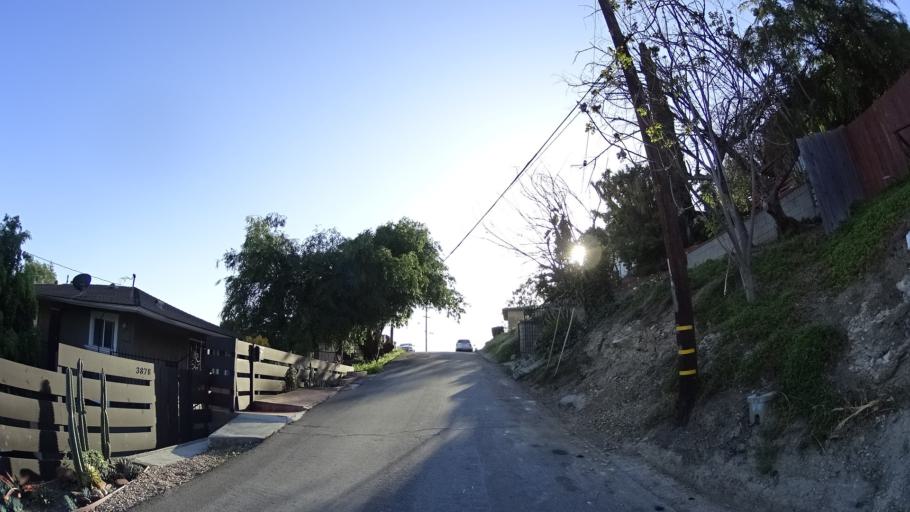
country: US
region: California
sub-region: Los Angeles County
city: Belvedere
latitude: 34.0500
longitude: -118.1824
